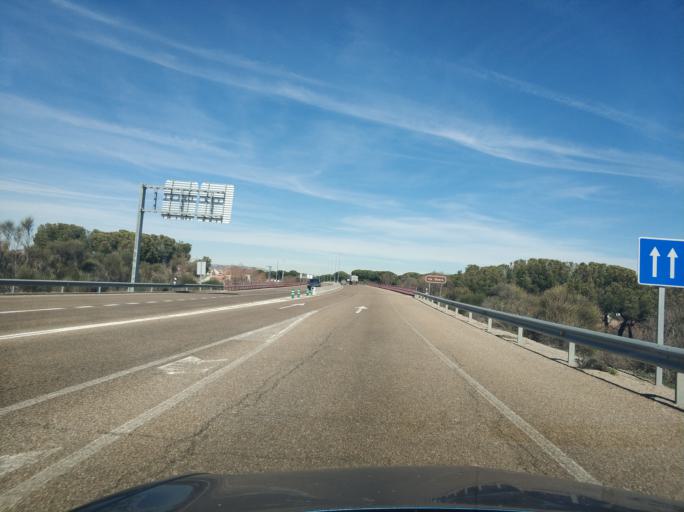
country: ES
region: Castille and Leon
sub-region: Provincia de Valladolid
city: Viana de Cega
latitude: 41.5503
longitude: -4.7871
